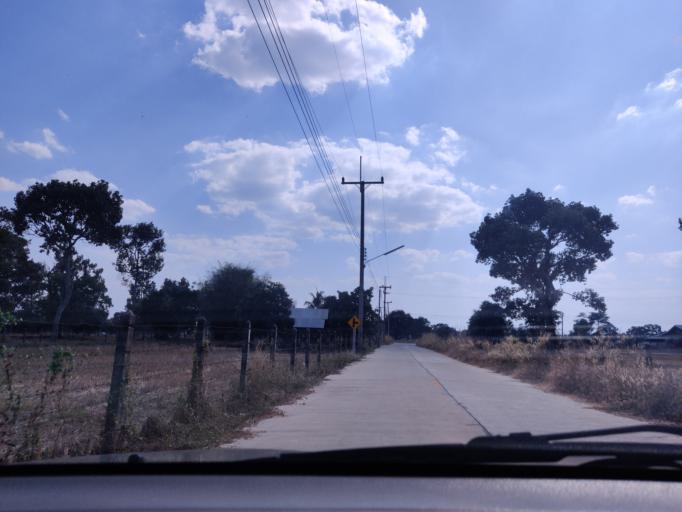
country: TH
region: Sisaket
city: Si Sa Ket
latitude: 15.0910
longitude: 104.3538
